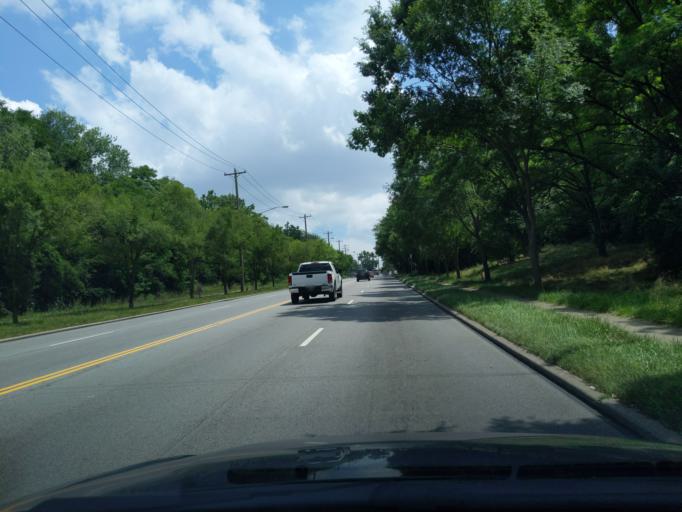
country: US
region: Ohio
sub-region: Hamilton County
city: Saint Bernard
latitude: 39.1372
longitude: -84.5225
